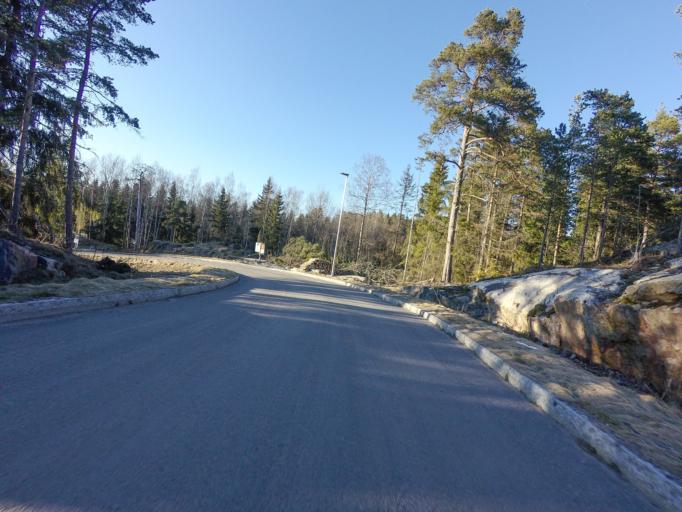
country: FI
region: Uusimaa
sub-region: Helsinki
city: Helsinki
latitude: 60.1728
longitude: 25.0255
